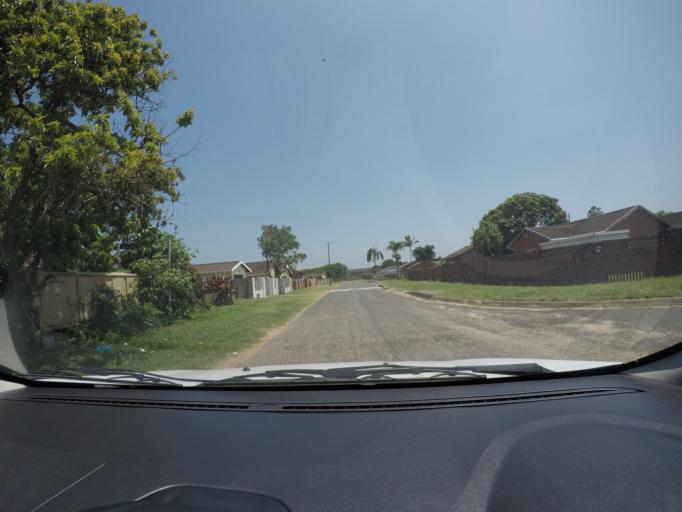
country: ZA
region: KwaZulu-Natal
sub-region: uThungulu District Municipality
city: eSikhawini
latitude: -28.8738
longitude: 31.9153
